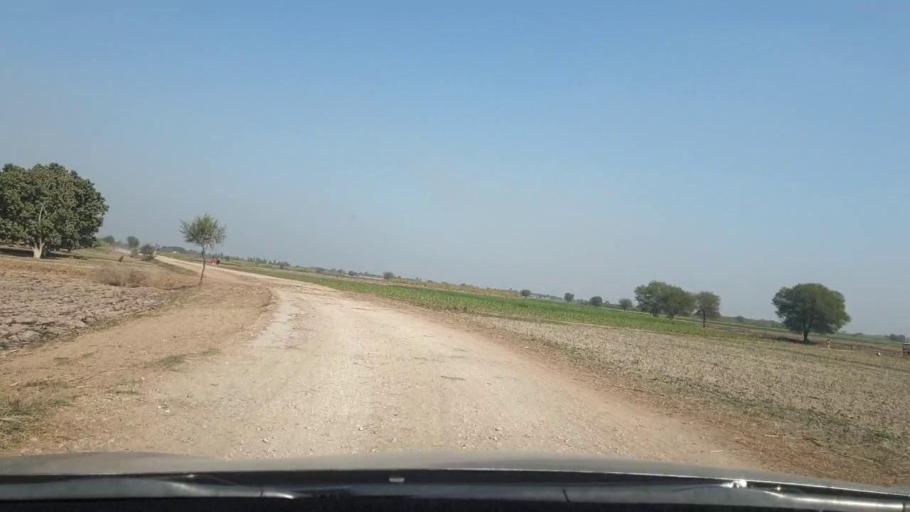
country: PK
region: Sindh
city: Tando Allahyar
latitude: 25.5990
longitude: 68.6419
